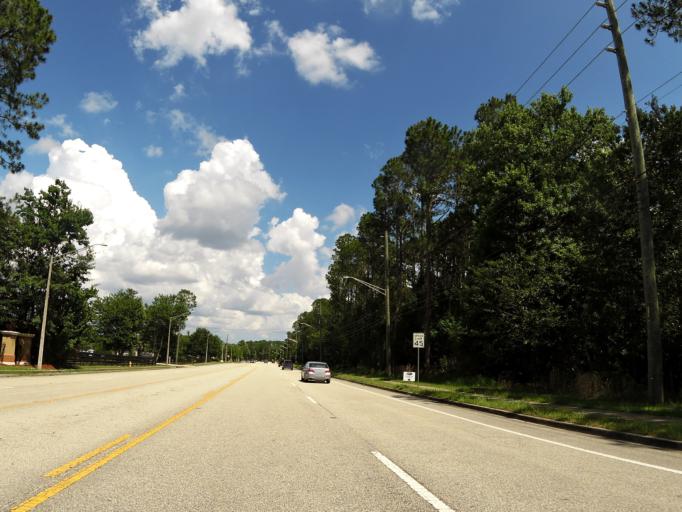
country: US
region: Florida
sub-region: Saint Johns County
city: Fruit Cove
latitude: 30.1513
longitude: -81.5824
